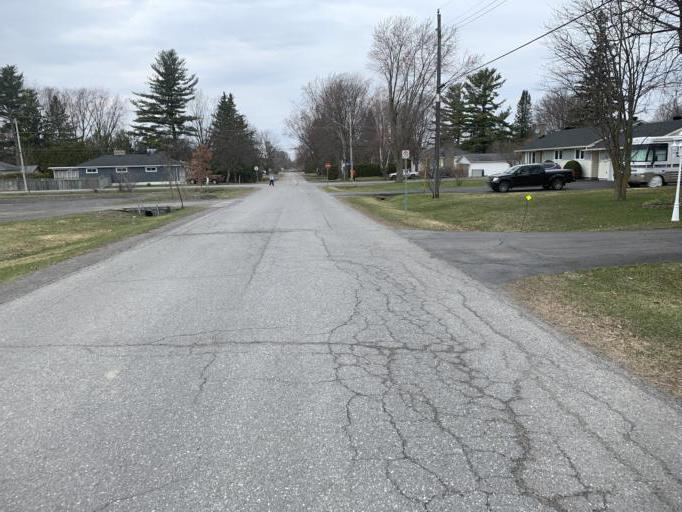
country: CA
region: Ontario
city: Bells Corners
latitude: 45.1886
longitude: -75.8267
